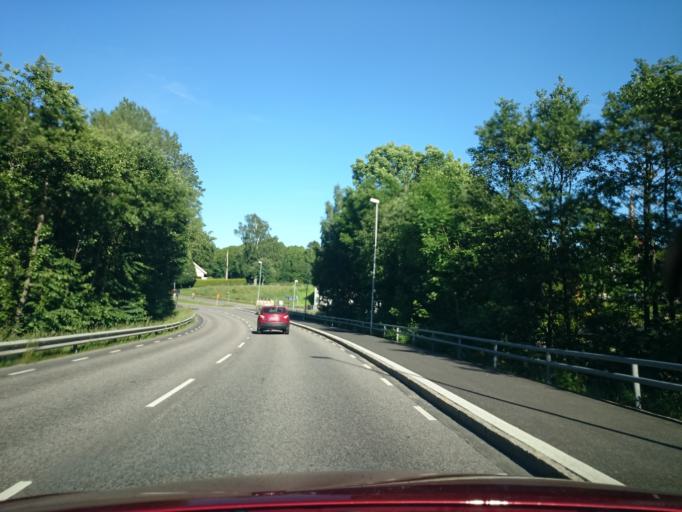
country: SE
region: Vaestra Goetaland
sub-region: Lerums Kommun
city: Lerum
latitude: 57.7767
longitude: 12.2811
